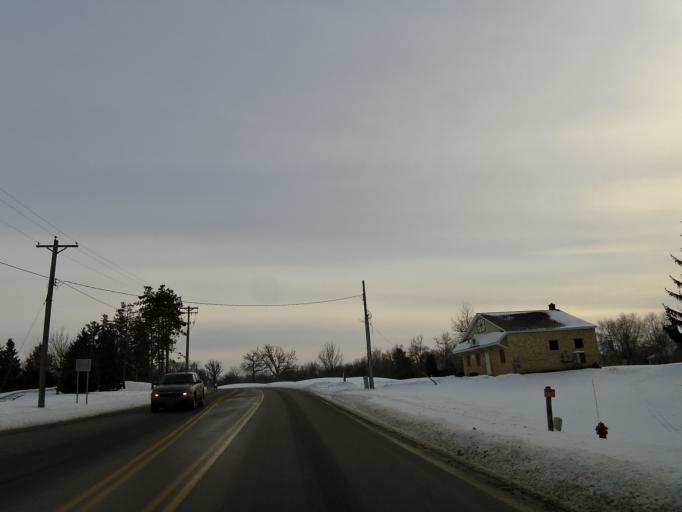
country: US
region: Minnesota
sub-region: Carver County
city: Victoria
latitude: 44.8518
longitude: -93.6597
